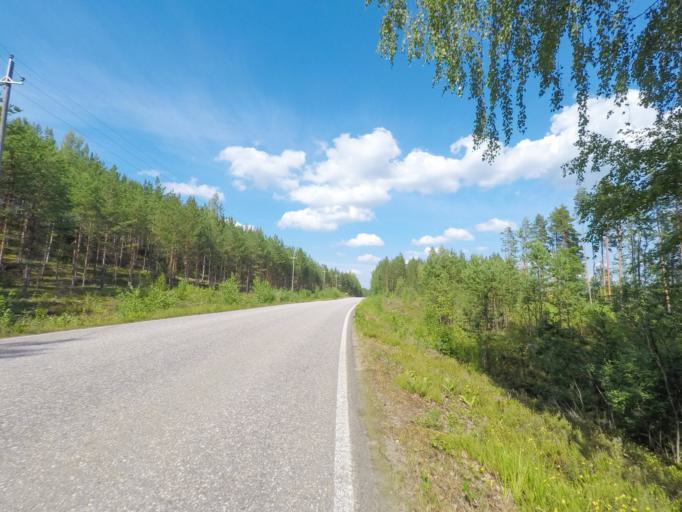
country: FI
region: Southern Savonia
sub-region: Mikkeli
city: Puumala
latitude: 61.4753
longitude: 28.1692
